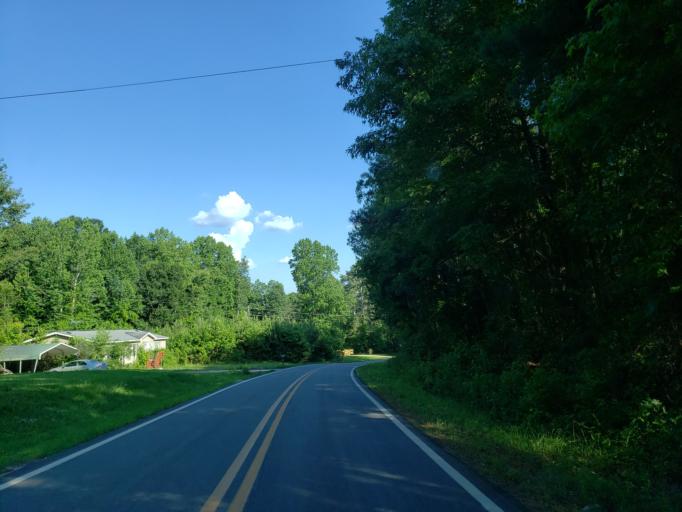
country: US
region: Georgia
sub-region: Haralson County
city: Bremen
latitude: 33.7010
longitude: -85.1013
